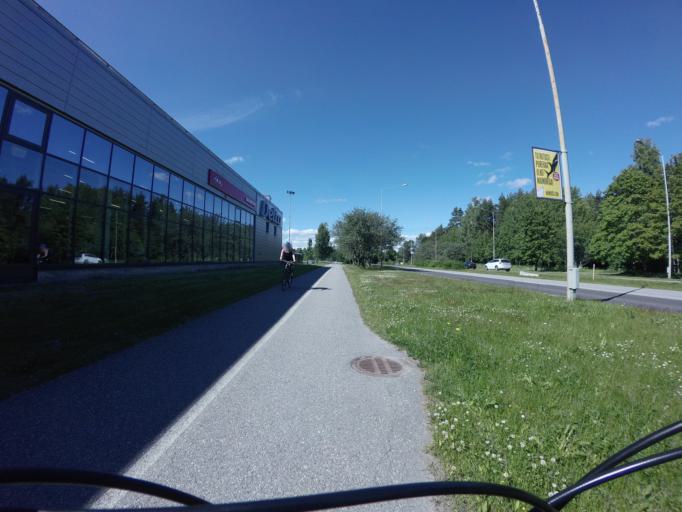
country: FI
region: Varsinais-Suomi
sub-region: Turku
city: Turku
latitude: 60.4718
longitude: 22.2650
